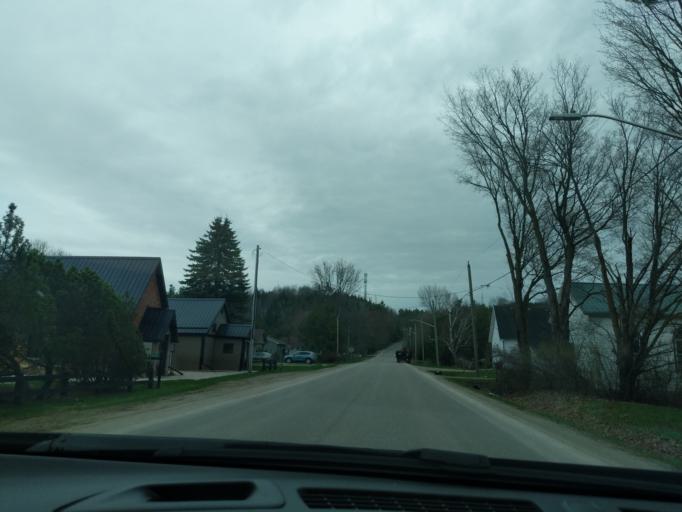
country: CA
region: Ontario
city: Orangeville
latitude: 44.0210
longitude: -79.9689
